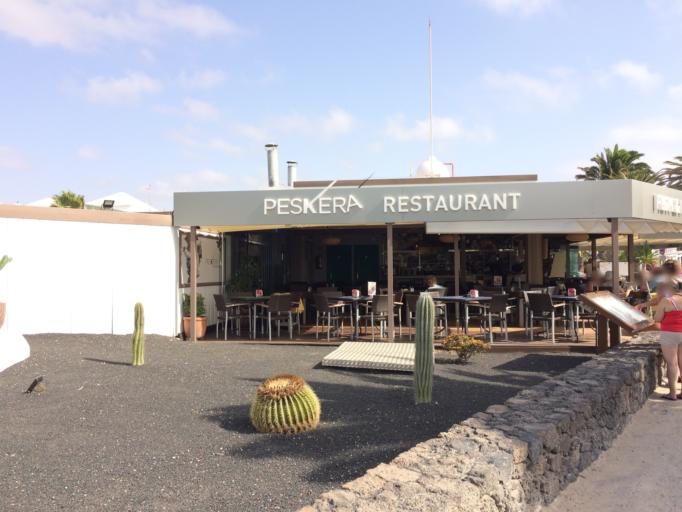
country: ES
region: Canary Islands
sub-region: Provincia de Las Palmas
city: Arrecife
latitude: 28.9992
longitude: -13.4883
